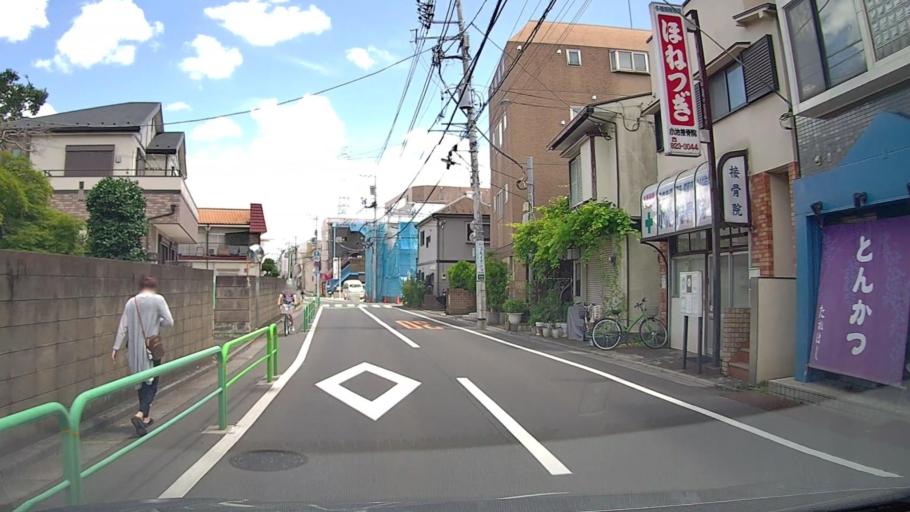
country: JP
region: Tokyo
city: Tanashicho
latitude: 35.7554
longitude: 139.5675
